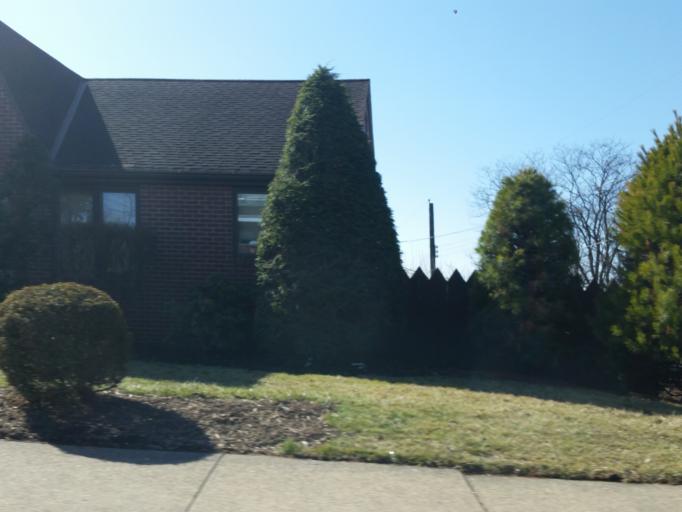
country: US
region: Pennsylvania
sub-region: Allegheny County
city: Ingram
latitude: 40.4478
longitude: -80.0619
